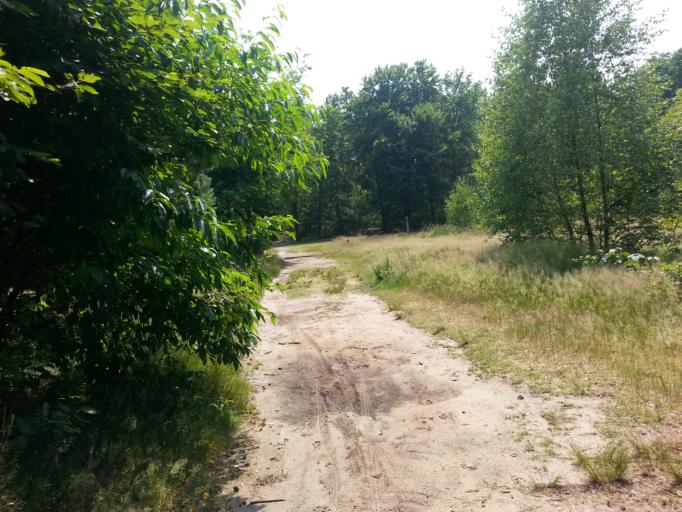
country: NL
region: Utrecht
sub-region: Gemeente Amersfoort
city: Randenbroek
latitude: 52.1202
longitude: 5.3876
